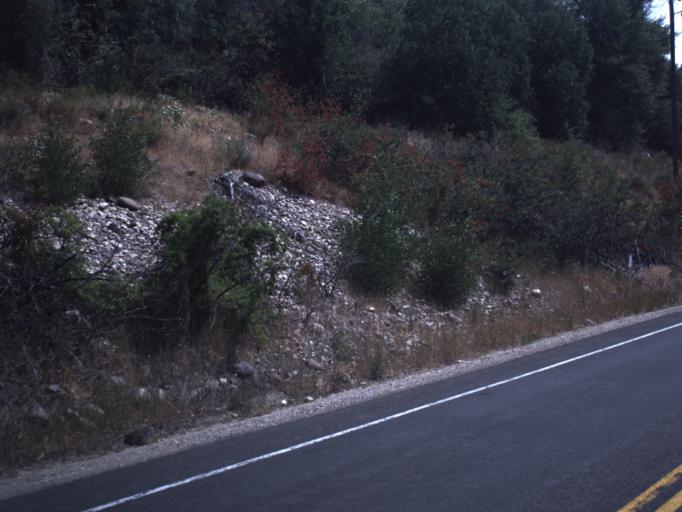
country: US
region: Utah
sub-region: Summit County
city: Francis
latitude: 40.5787
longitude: -111.2191
